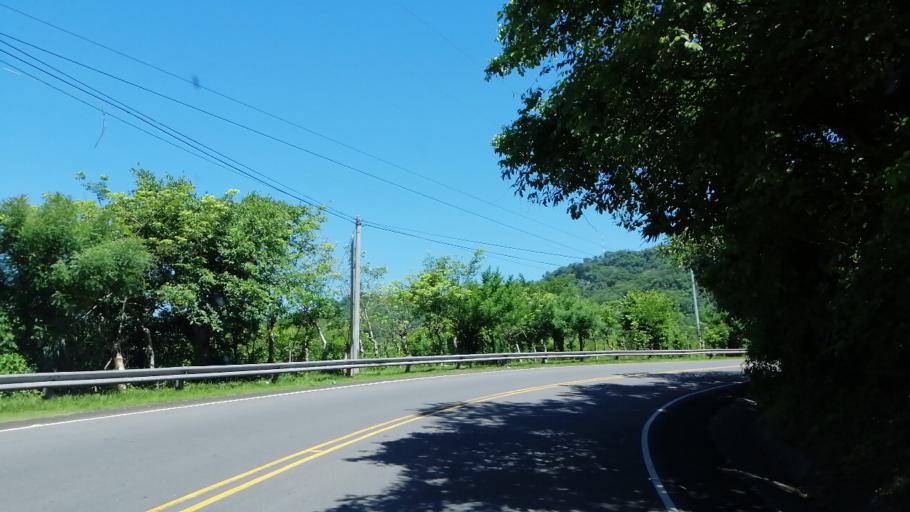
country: SV
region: Morazan
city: Cacaopera
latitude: 13.7989
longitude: -88.1471
